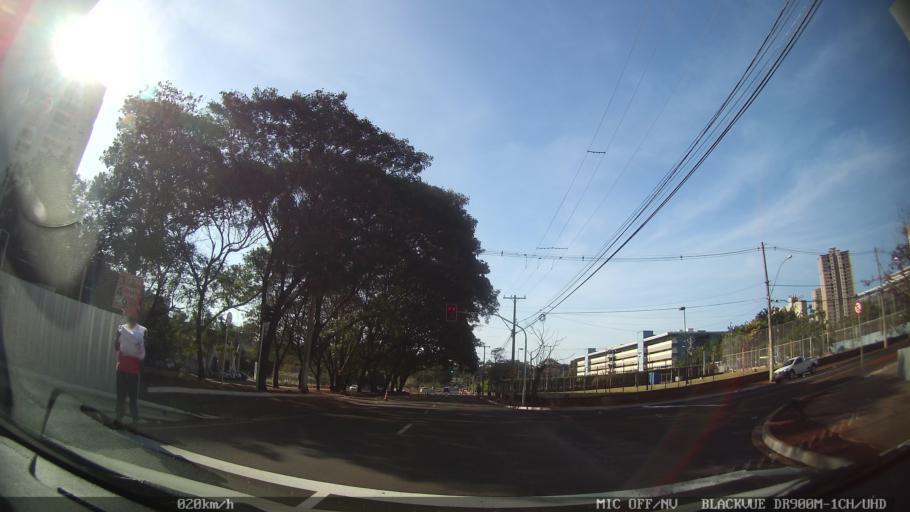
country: BR
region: Sao Paulo
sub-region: Ribeirao Preto
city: Ribeirao Preto
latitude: -21.2169
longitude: -47.8193
